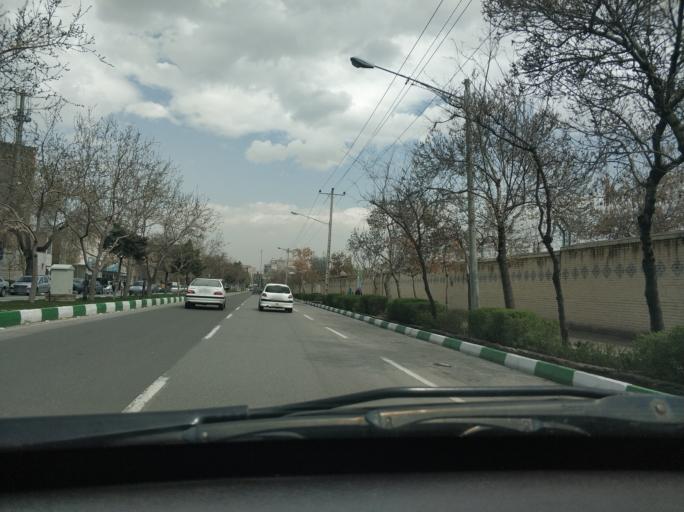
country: IR
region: Razavi Khorasan
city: Mashhad
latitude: 36.2818
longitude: 59.5776
